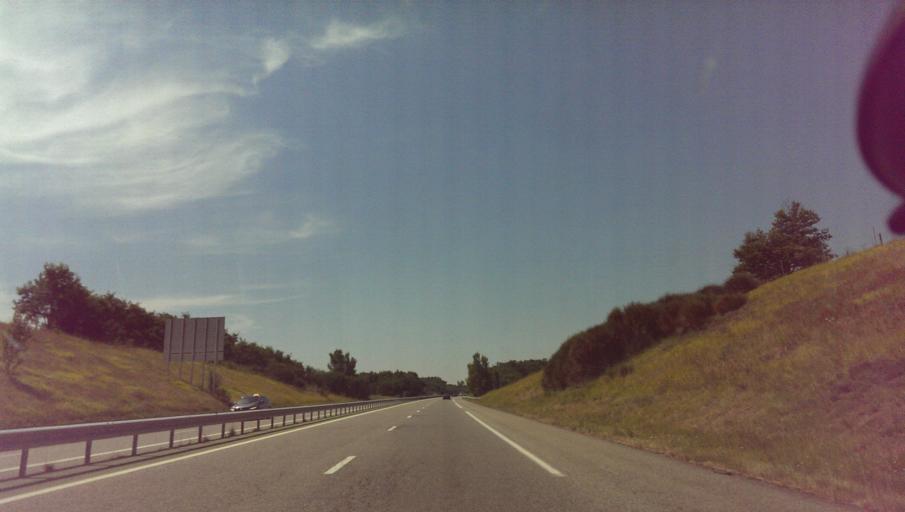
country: FR
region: Midi-Pyrenees
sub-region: Departement de la Haute-Garonne
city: Villenouvelle
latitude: 43.3987
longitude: 1.6393
